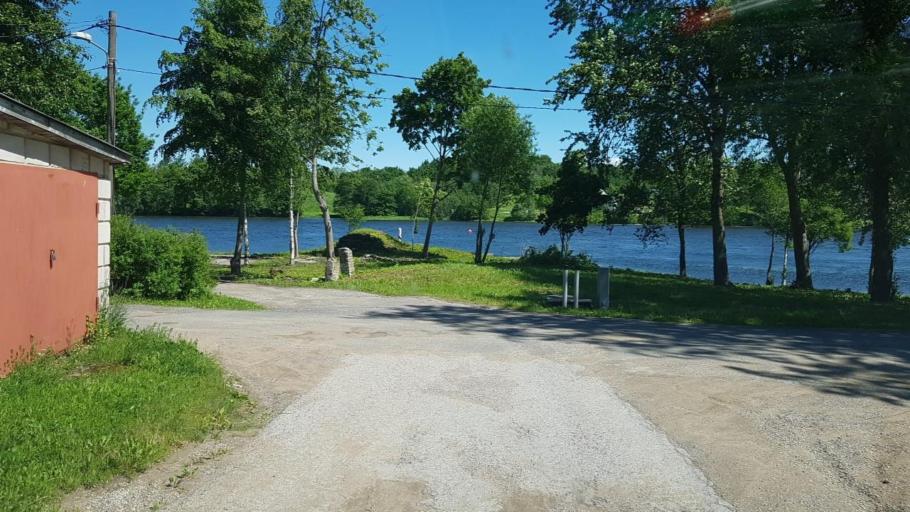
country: EE
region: Ida-Virumaa
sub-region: Narva linn
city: Narva
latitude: 59.3894
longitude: 28.1997
